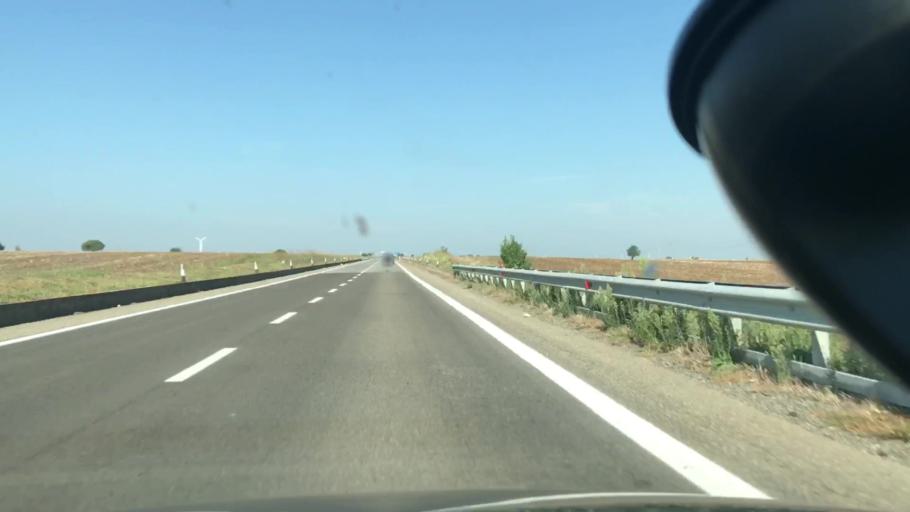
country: IT
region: Basilicate
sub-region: Provincia di Potenza
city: Montemilone
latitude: 40.9890
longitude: 15.9046
